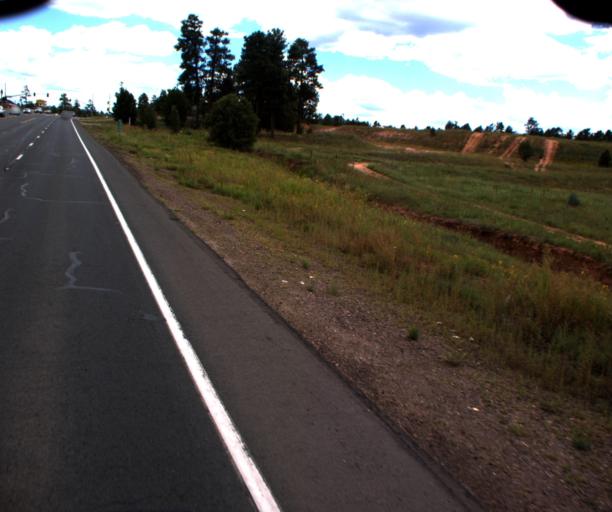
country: US
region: Arizona
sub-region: Navajo County
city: Show Low
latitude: 34.2110
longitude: -110.0260
